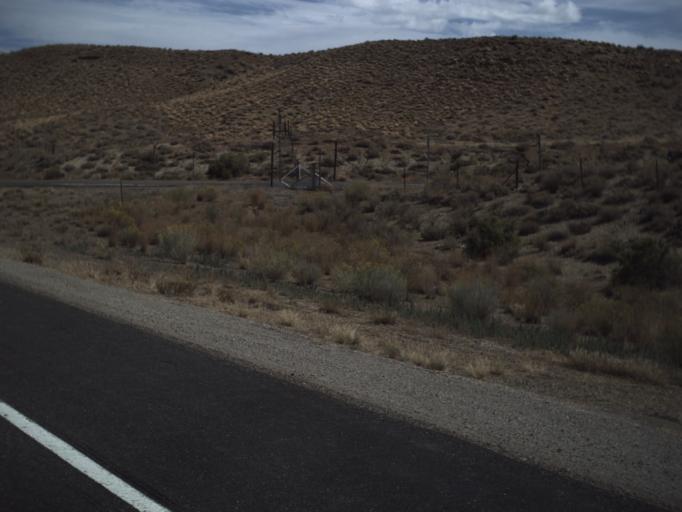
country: US
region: Utah
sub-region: Grand County
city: Moab
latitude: 38.9610
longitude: -109.7229
